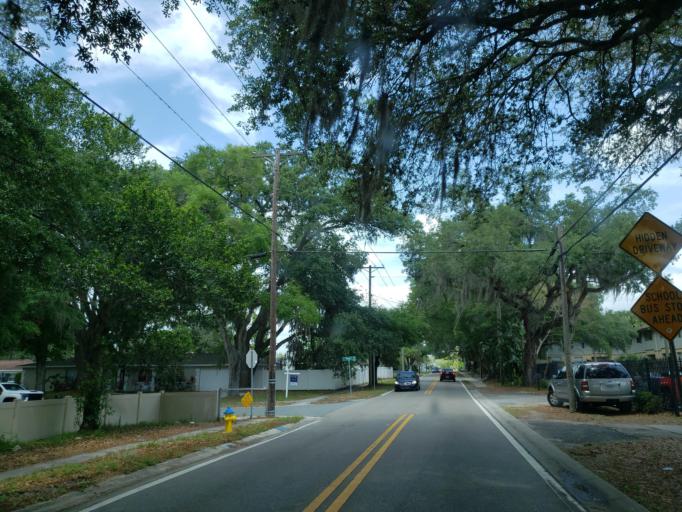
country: US
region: Florida
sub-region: Hillsborough County
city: Brandon
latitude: 27.9399
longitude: -82.2940
